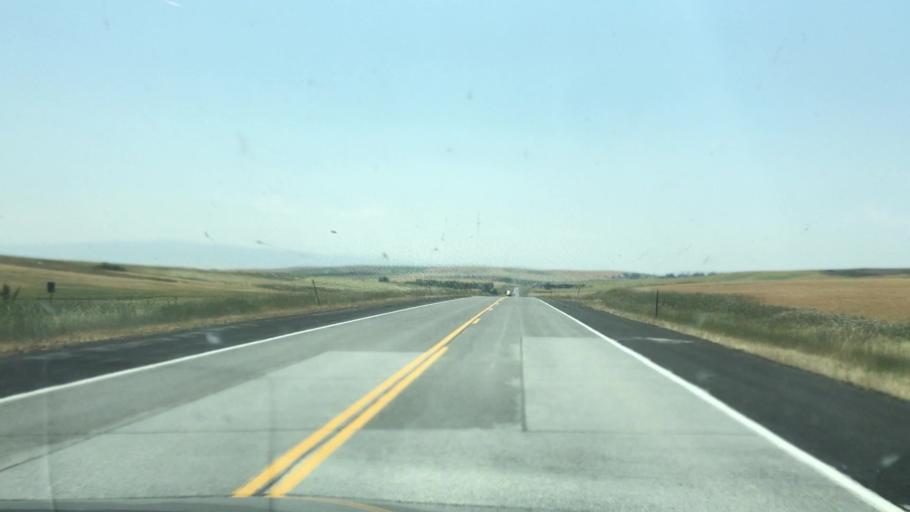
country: US
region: Idaho
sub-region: Lewis County
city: Nezperce
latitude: 46.0918
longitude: -116.3481
